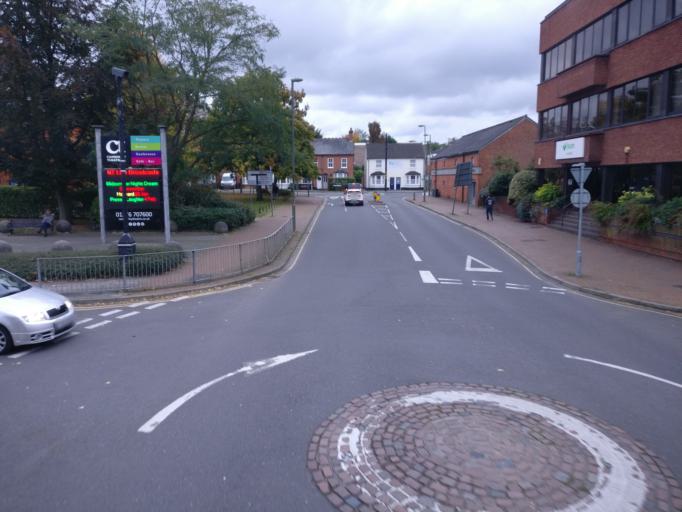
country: GB
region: England
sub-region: Surrey
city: Camberley
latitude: 51.3380
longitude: -0.7427
